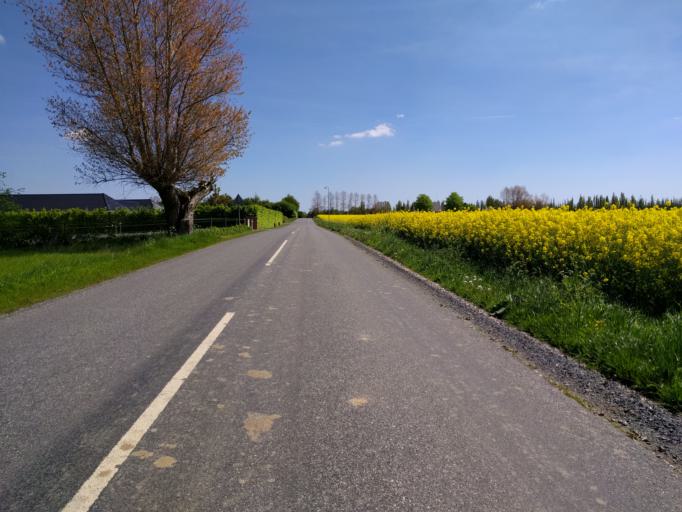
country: DK
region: Zealand
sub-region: Guldborgsund Kommune
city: Nykobing Falster
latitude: 54.7401
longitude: 11.9902
